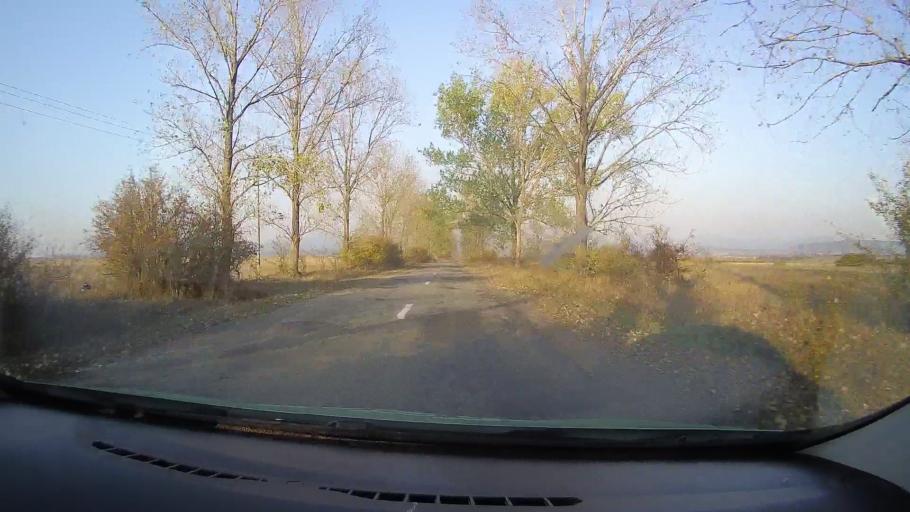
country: RO
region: Arad
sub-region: Comuna Barsa
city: Barsa
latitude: 46.3718
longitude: 22.0462
